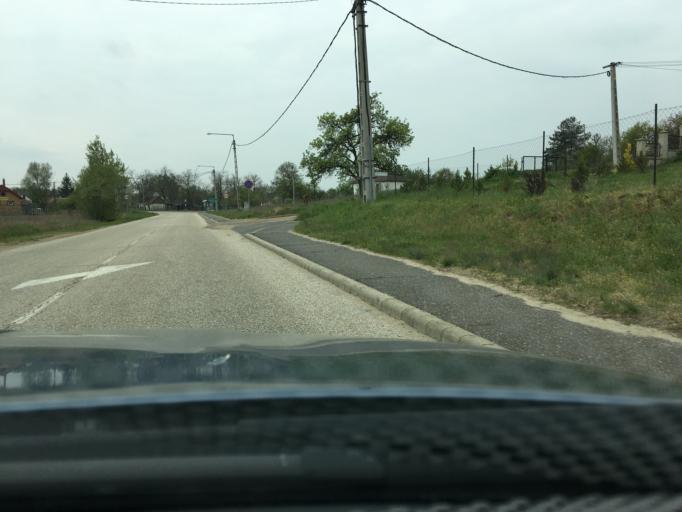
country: HU
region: Hajdu-Bihar
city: Hajdusamson
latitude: 47.5696
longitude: 21.7695
